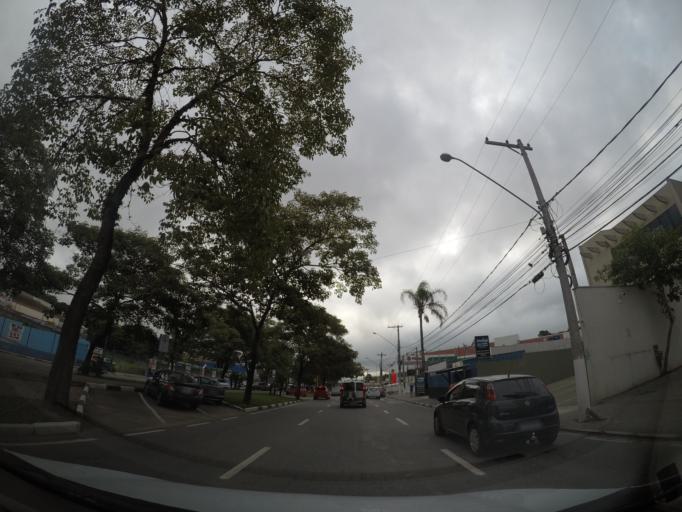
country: BR
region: Sao Paulo
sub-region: Aruja
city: Aruja
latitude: -23.3953
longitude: -46.3288
